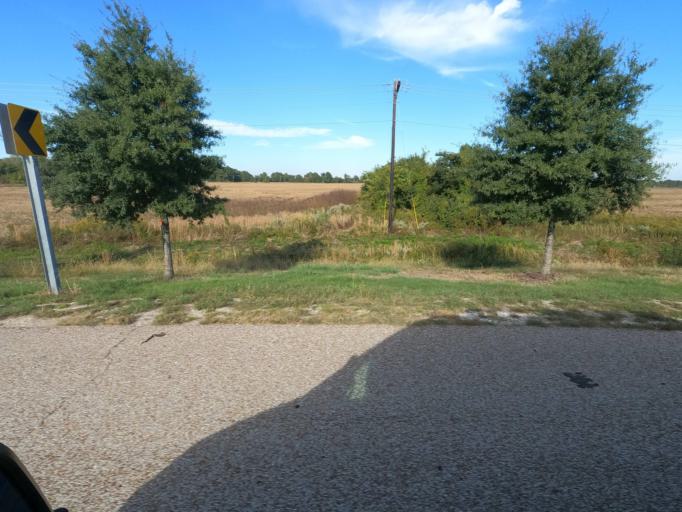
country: US
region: Arkansas
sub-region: Crittenden County
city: West Memphis
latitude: 35.1668
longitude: -90.1745
